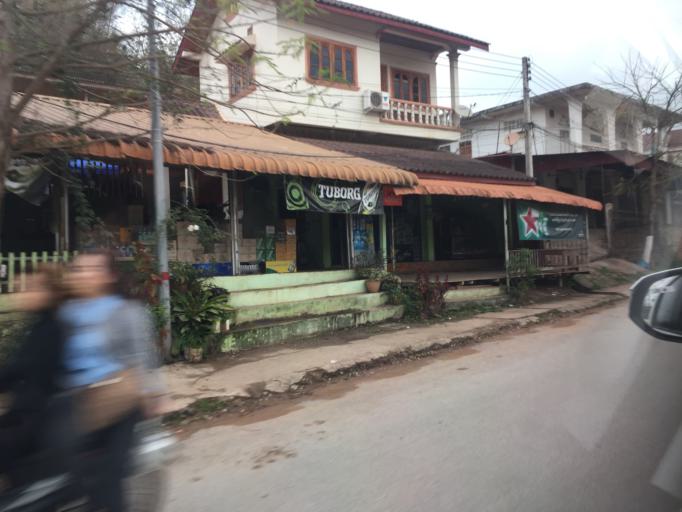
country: LA
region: Oudomxai
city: Muang Xay
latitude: 20.6872
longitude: 101.9875
